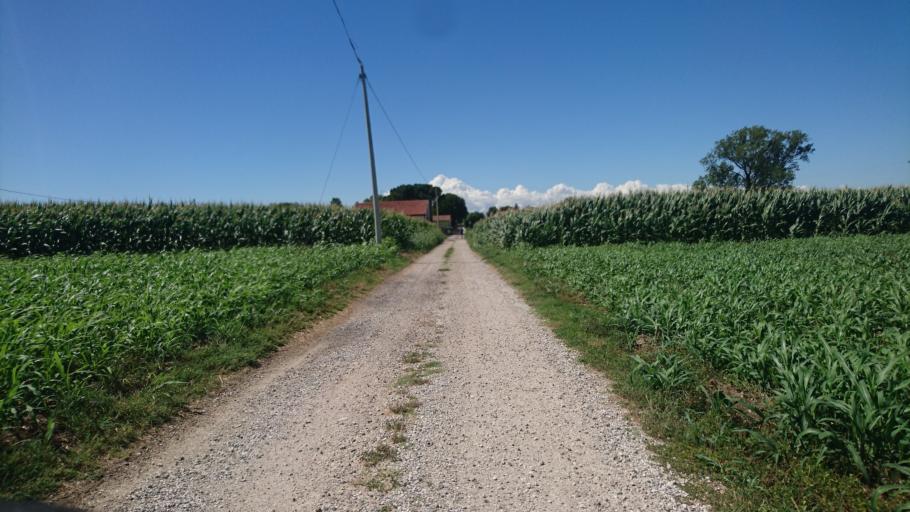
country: IT
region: Veneto
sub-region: Provincia di Padova
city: Pontelongo
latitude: 45.2563
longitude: 12.0191
